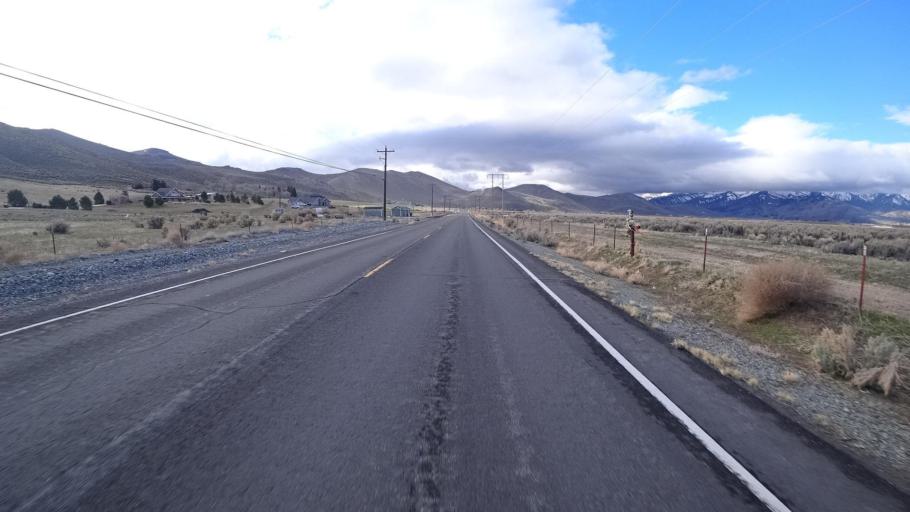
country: US
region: Nevada
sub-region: Carson City
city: Carson City
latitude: 39.2615
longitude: -119.7567
